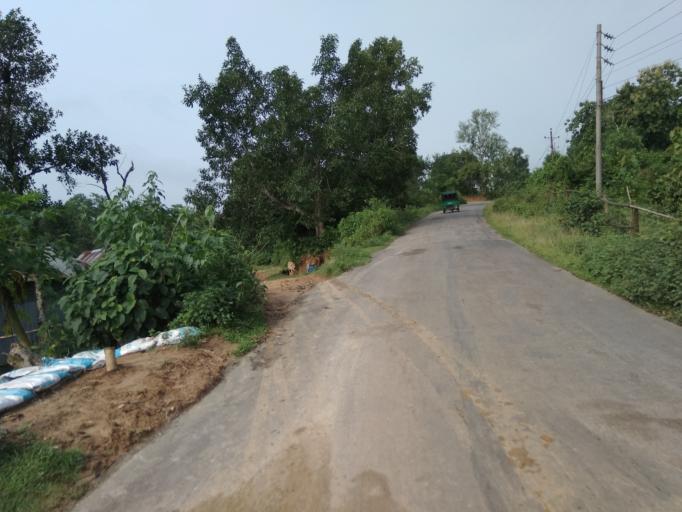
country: BD
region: Chittagong
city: Khagrachhari
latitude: 23.0118
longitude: 92.0137
